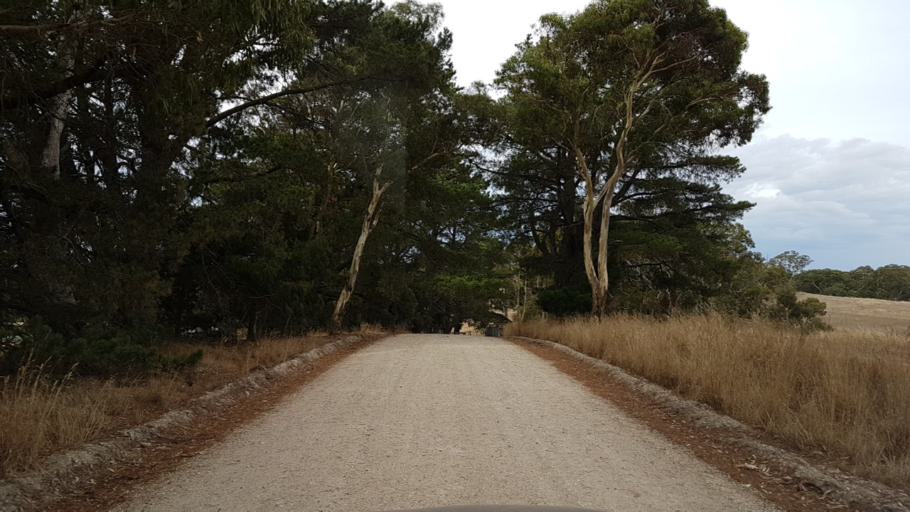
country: AU
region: South Australia
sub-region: Adelaide Hills
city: Birdwood
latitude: -34.7619
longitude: 138.9932
